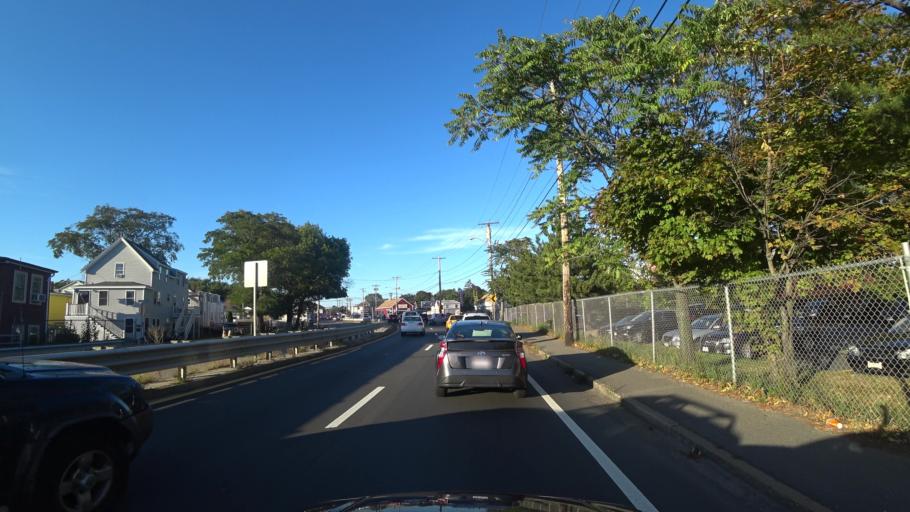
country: US
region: Massachusetts
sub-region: Suffolk County
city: Revere
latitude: 42.4161
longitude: -70.9912
